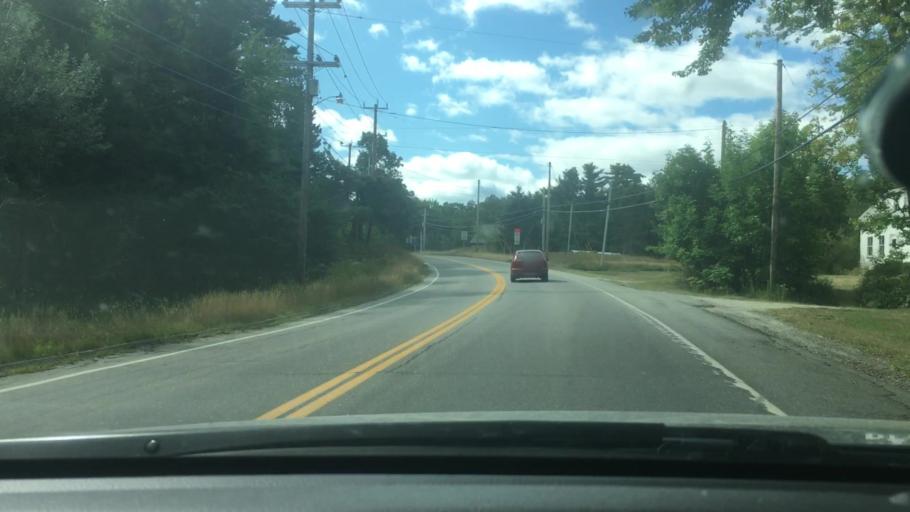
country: US
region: Maine
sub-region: Hancock County
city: Trenton
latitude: 44.3745
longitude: -68.3321
